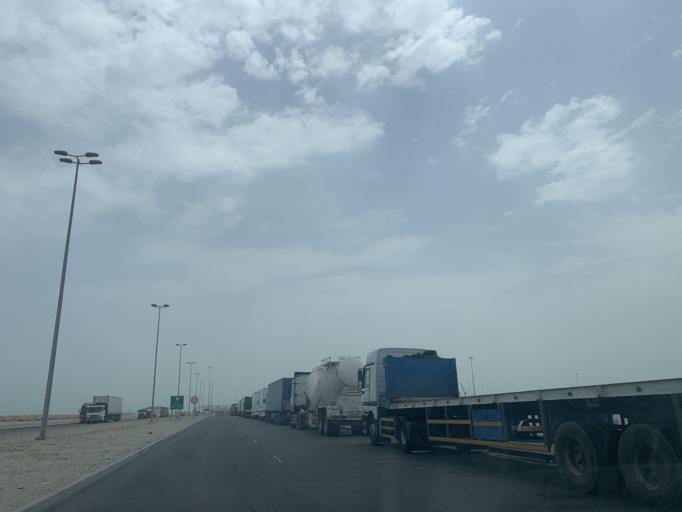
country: BH
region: Muharraq
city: Al Hadd
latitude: 26.2010
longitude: 50.7095
